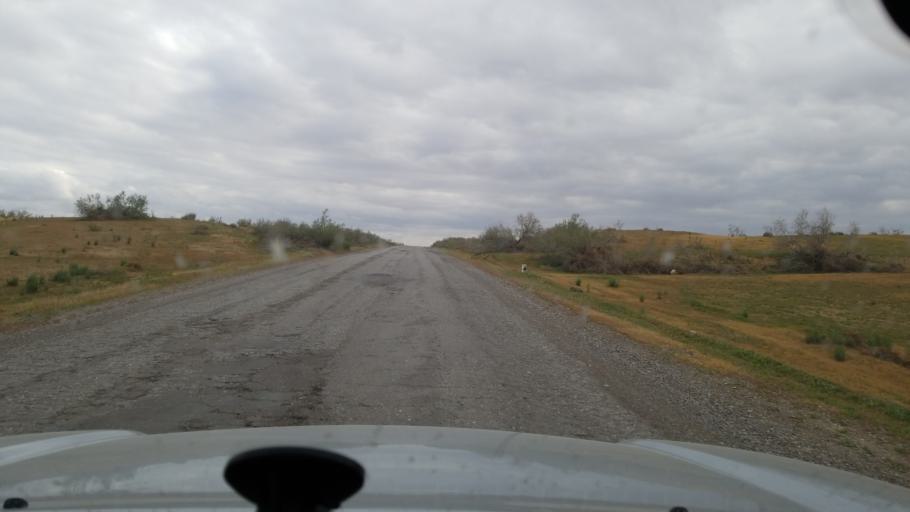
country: TM
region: Mary
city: Serhetabat
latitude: 36.0352
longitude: 62.6149
